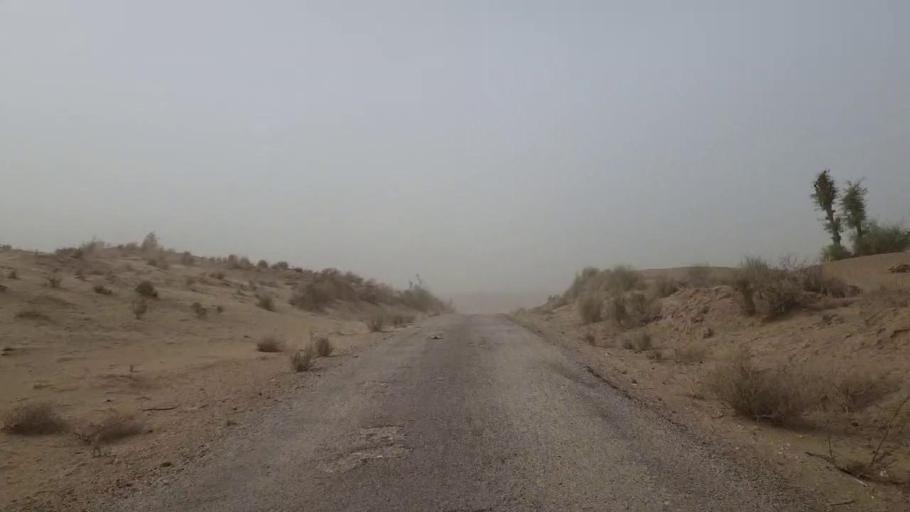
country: PK
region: Sindh
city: Islamkot
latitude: 24.5657
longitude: 70.3628
